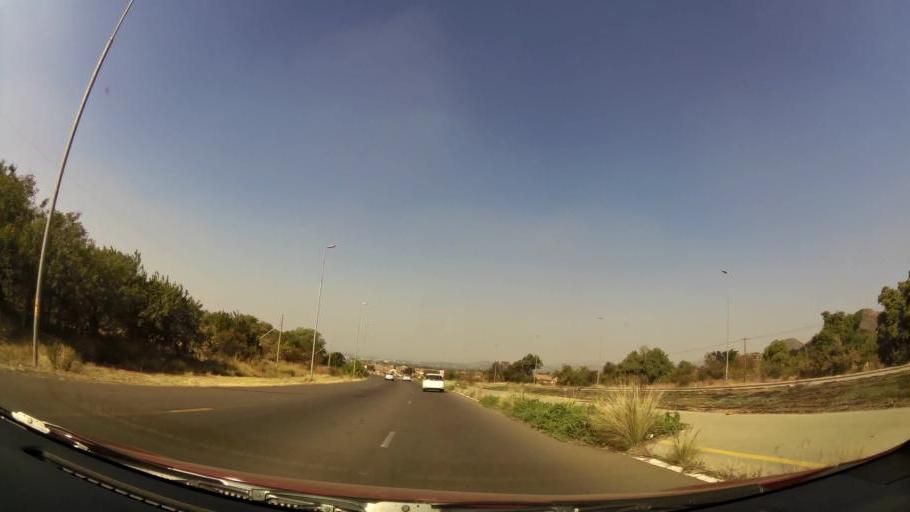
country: ZA
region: North-West
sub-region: Bojanala Platinum District Municipality
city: Rustenburg
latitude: -25.6384
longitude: 27.1968
